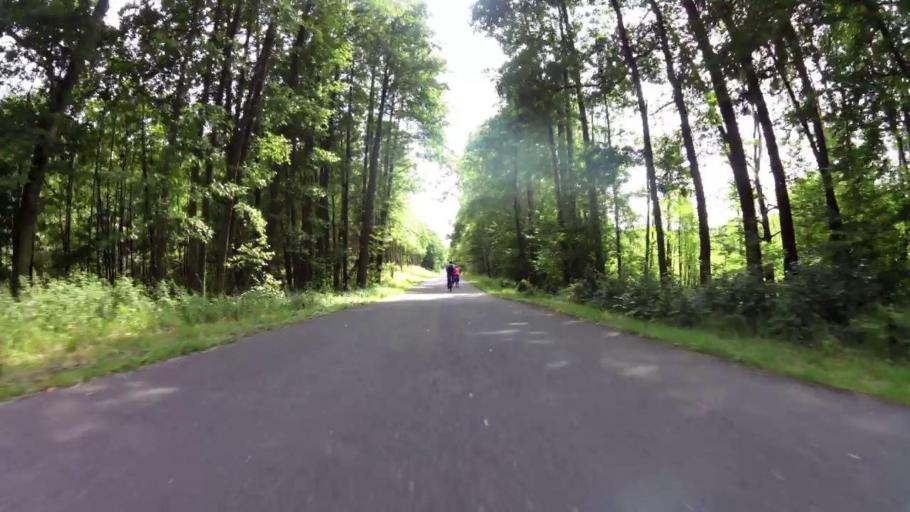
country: PL
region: West Pomeranian Voivodeship
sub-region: Powiat choszczenski
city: Drawno
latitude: 53.3428
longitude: 15.7039
